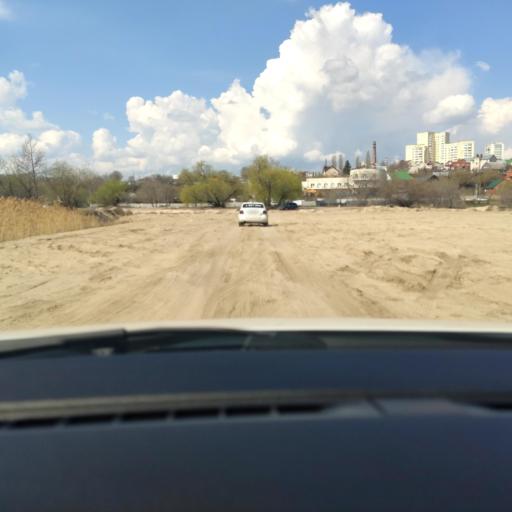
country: RU
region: Voronezj
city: Voronezh
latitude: 51.6385
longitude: 39.2125
